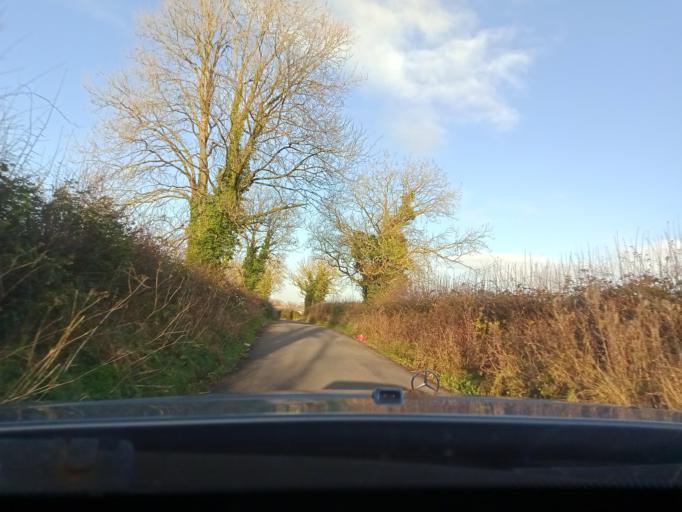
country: IE
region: Leinster
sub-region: Kilkenny
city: Callan
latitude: 52.5322
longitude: -7.3785
